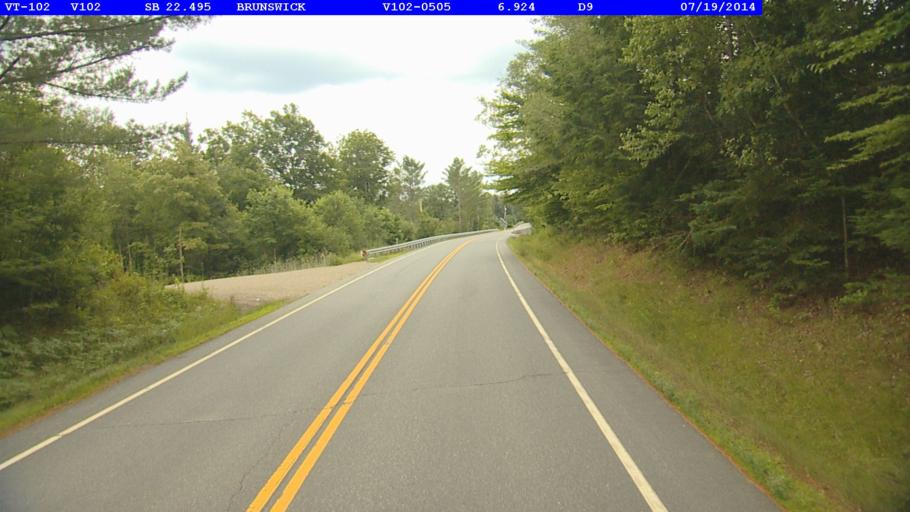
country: US
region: New Hampshire
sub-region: Coos County
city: Stratford
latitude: 44.7469
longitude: -71.6319
